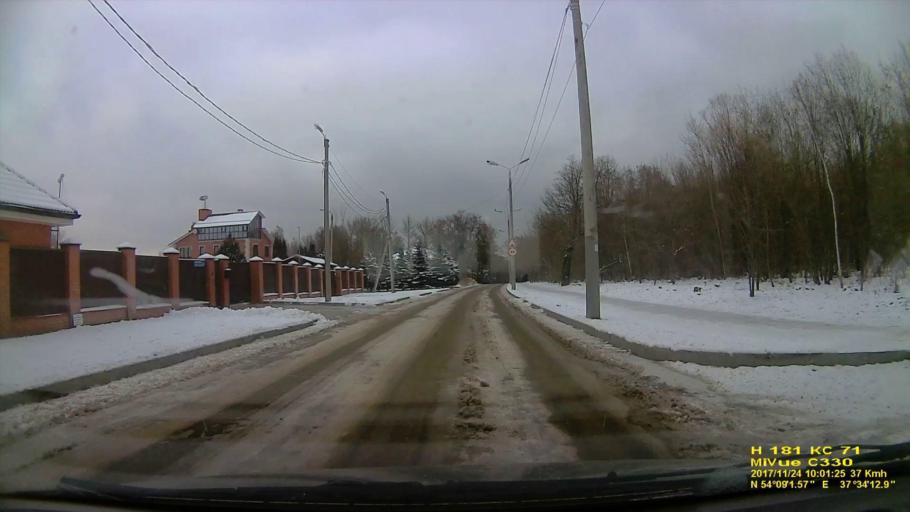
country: RU
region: Tula
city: Mendeleyevskiy
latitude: 54.1505
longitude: 37.5703
